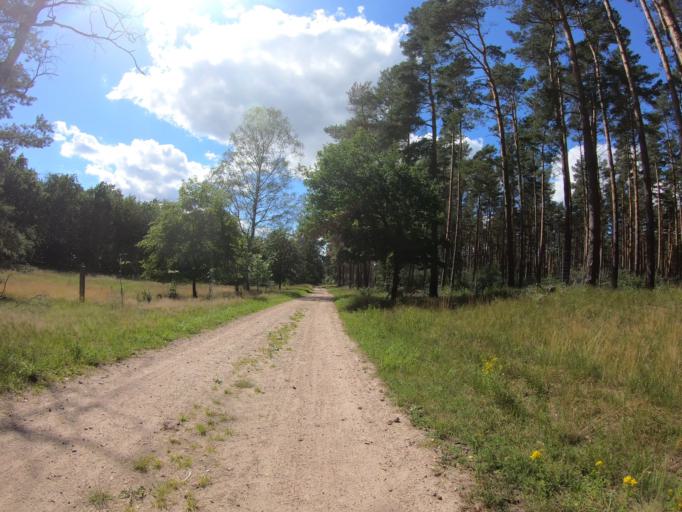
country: DE
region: Lower Saxony
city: Wagenhoff
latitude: 52.5040
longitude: 10.4599
